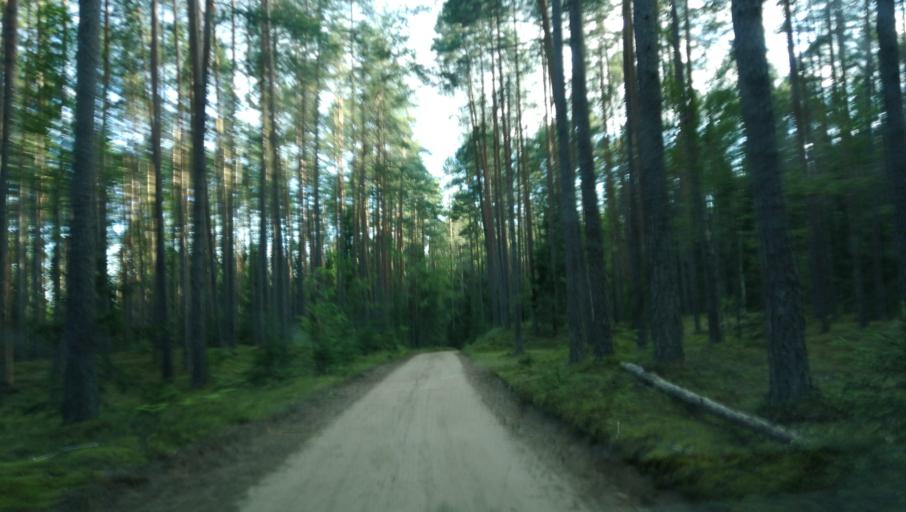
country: LV
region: Cesu Rajons
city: Cesis
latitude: 57.2942
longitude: 25.2059
